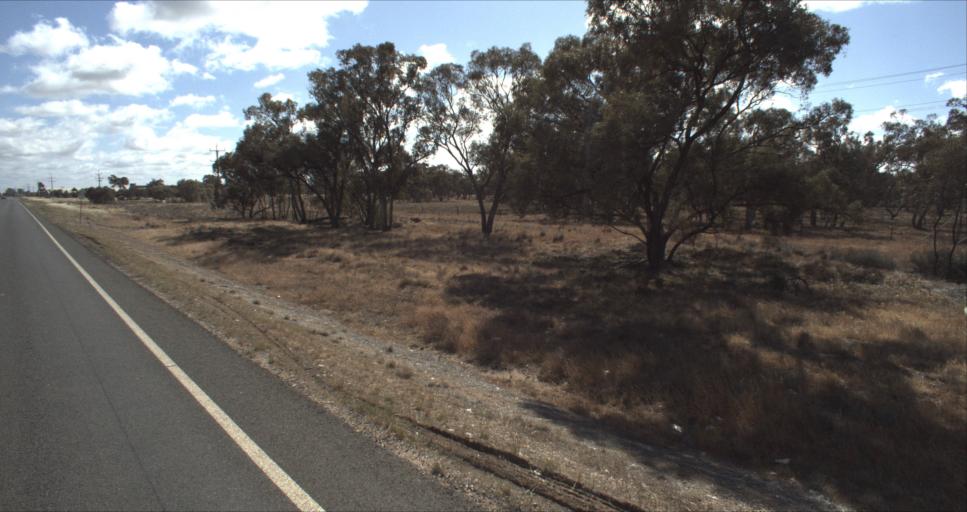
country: AU
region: New South Wales
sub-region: Murrumbidgee Shire
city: Darlington Point
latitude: -34.5213
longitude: 146.1757
